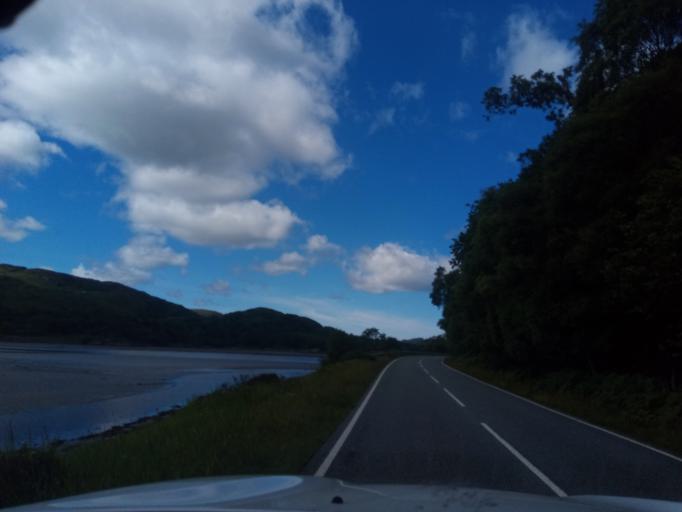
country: GB
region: Scotland
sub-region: Argyll and Bute
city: Isle Of Mull
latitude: 56.7900
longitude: -5.7734
